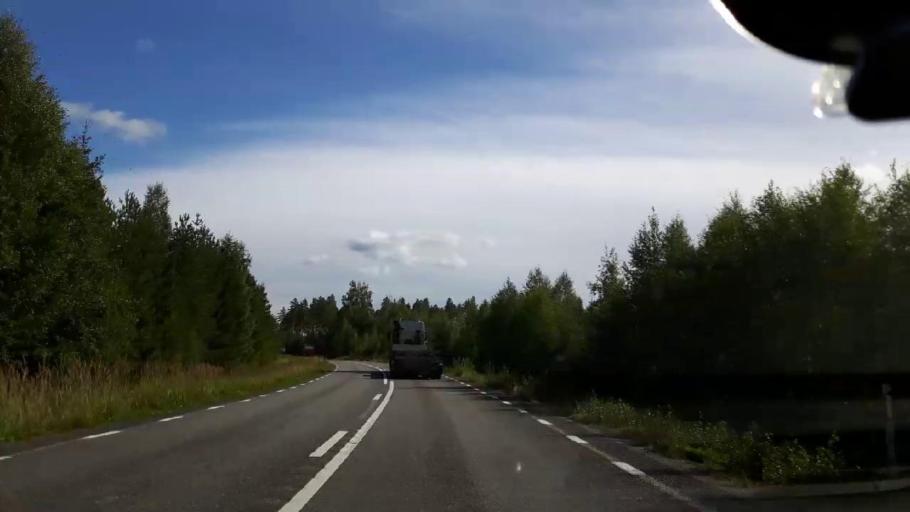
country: SE
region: Jaemtland
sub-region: Braecke Kommun
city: Braecke
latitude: 63.1907
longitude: 15.4420
